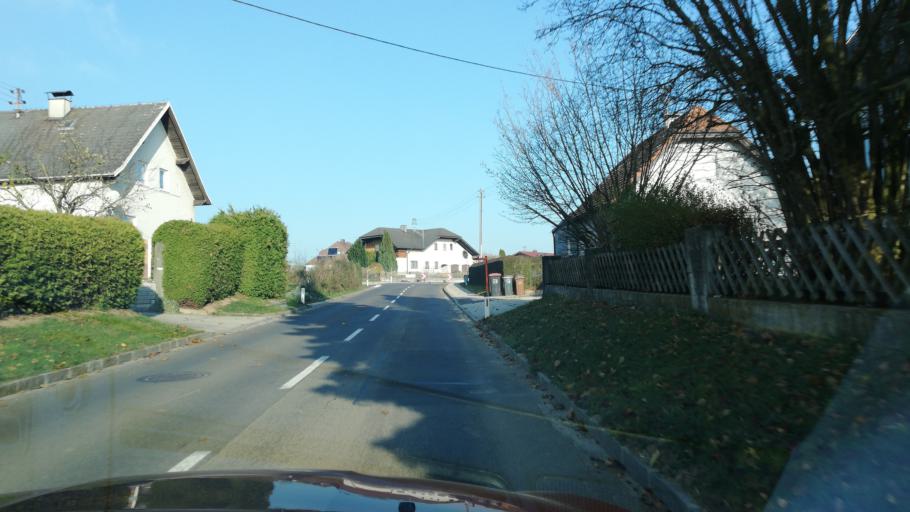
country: AT
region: Upper Austria
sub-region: Wels-Land
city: Buchkirchen
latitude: 48.2298
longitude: 14.0268
